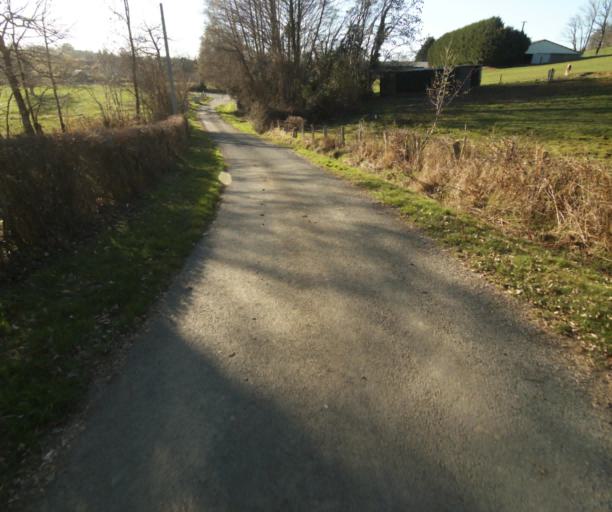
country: FR
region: Limousin
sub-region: Departement de la Correze
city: Seilhac
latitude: 45.3564
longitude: 1.6996
